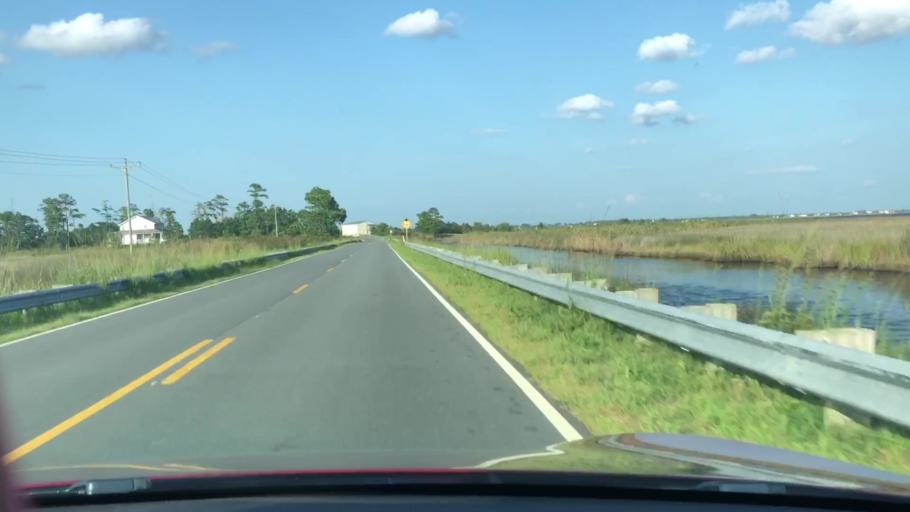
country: US
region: North Carolina
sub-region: Dare County
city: Wanchese
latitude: 35.6944
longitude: -75.7774
